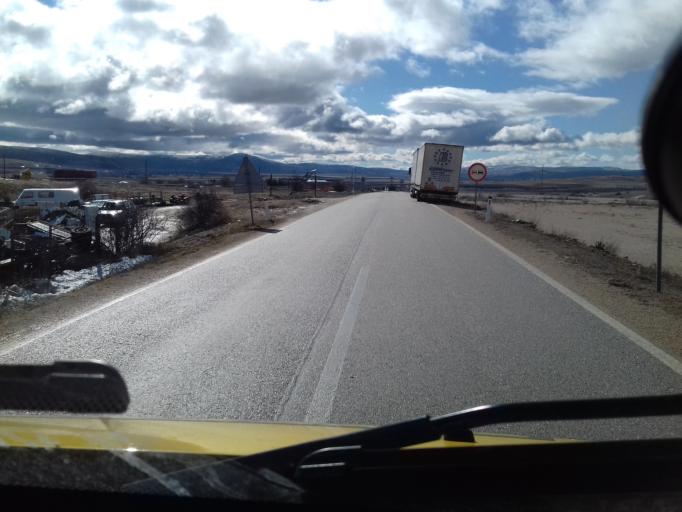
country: BA
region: Federation of Bosnia and Herzegovina
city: Tomislavgrad
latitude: 43.7717
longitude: 17.2336
